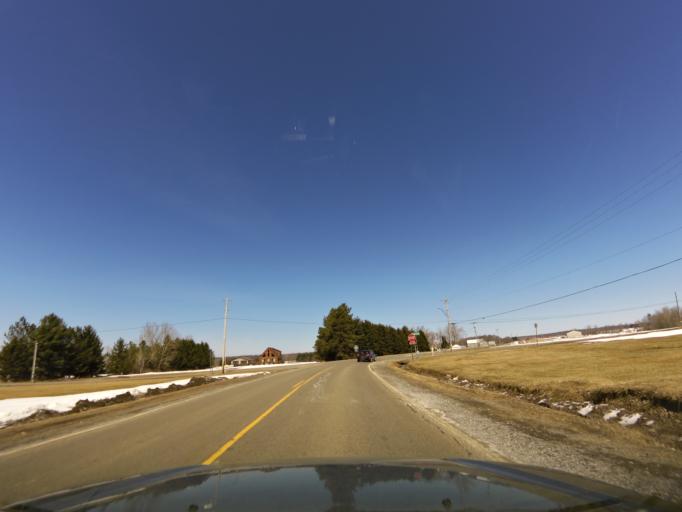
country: US
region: New York
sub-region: Cattaraugus County
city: Yorkshire
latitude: 42.5509
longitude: -78.4561
